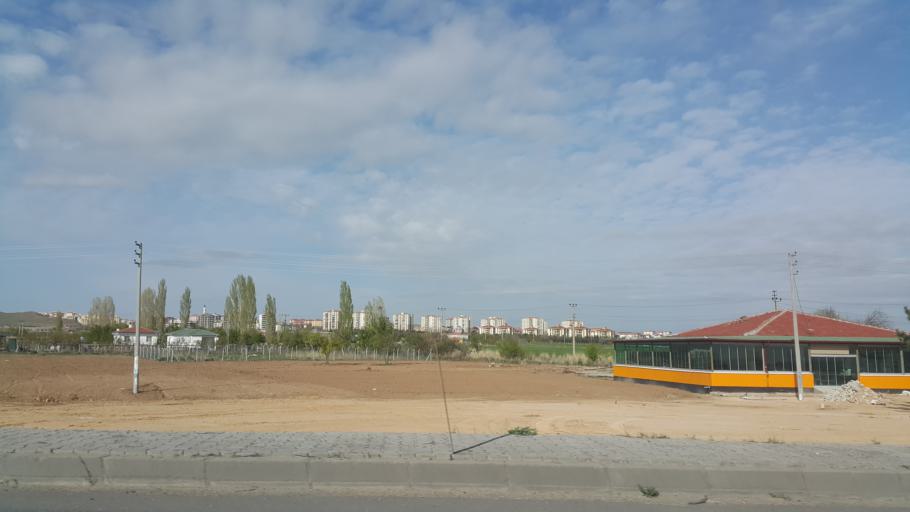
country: TR
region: Aksaray
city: Aksaray
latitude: 38.4074
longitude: 33.9780
